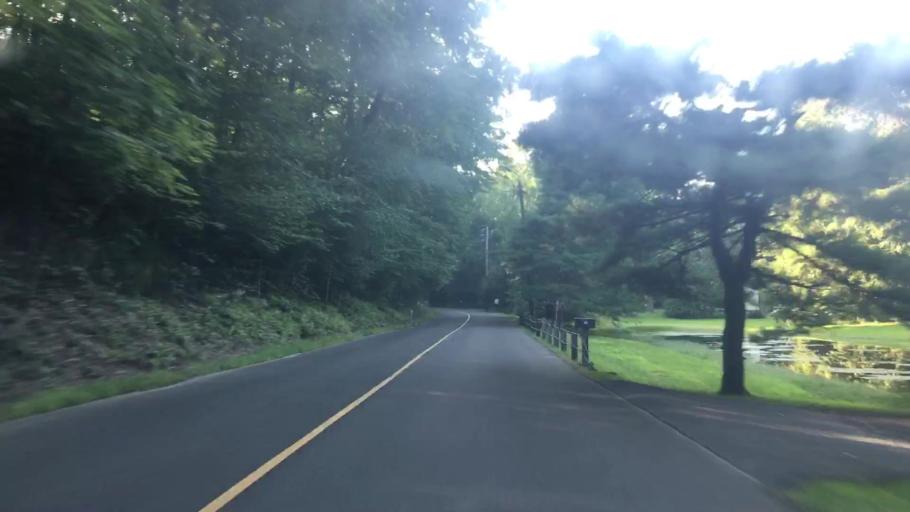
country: US
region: Connecticut
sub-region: Middlesex County
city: Chester Center
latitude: 41.3948
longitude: -72.4516
